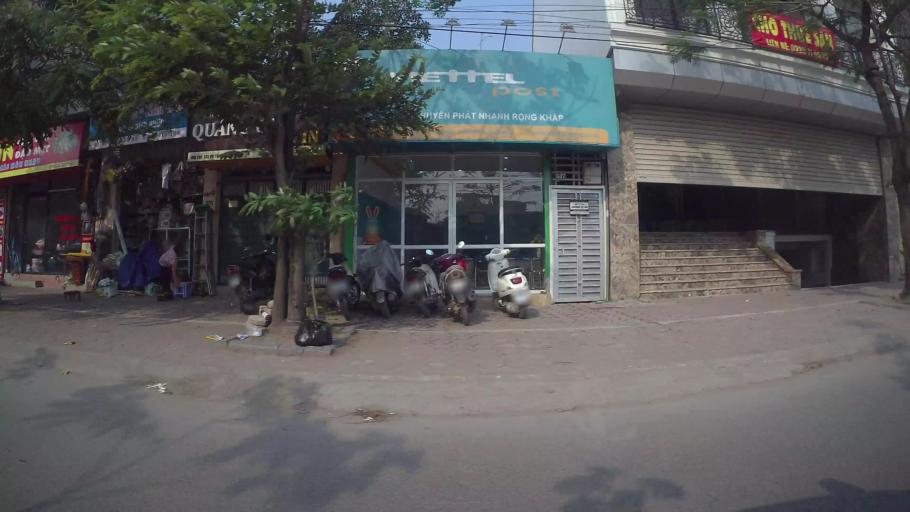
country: VN
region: Ha Noi
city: Thanh Xuan
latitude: 20.9852
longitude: 105.8148
